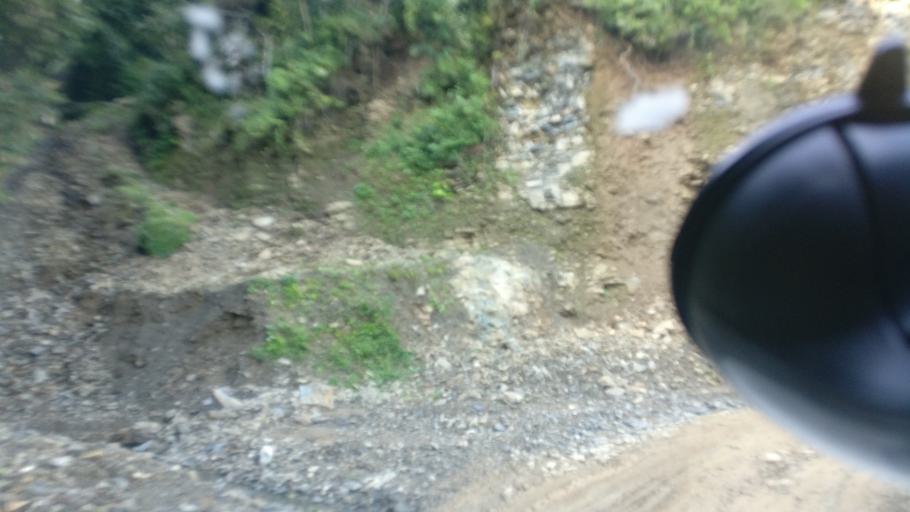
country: NP
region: Western Region
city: Baglung
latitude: 28.1445
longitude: 83.6547
